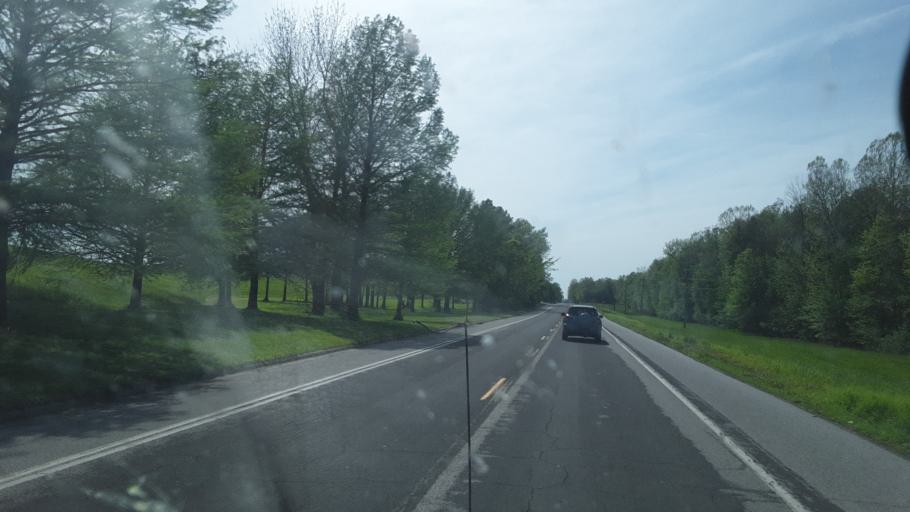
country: US
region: Illinois
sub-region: Jackson County
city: Carbondale
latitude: 37.7006
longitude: -89.2250
